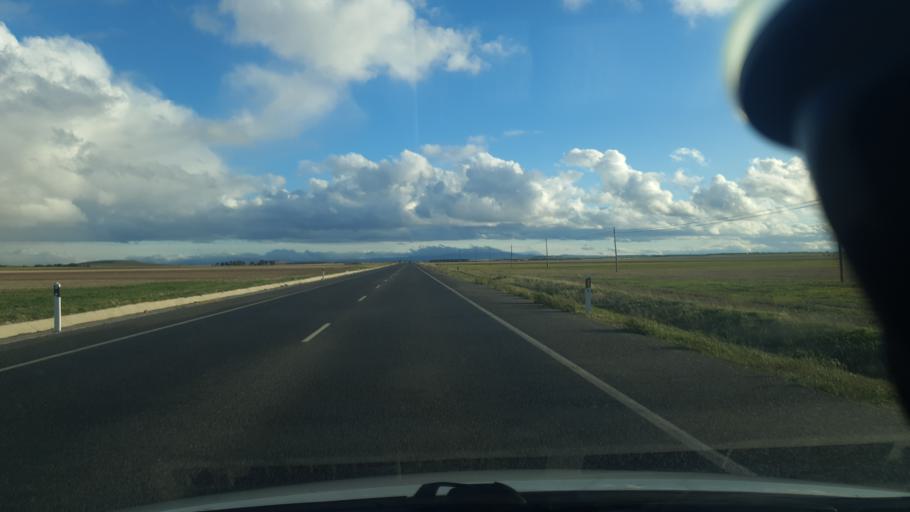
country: ES
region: Castille and Leon
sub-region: Provincia de Segovia
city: Codorniz
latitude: 41.0332
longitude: -4.6193
